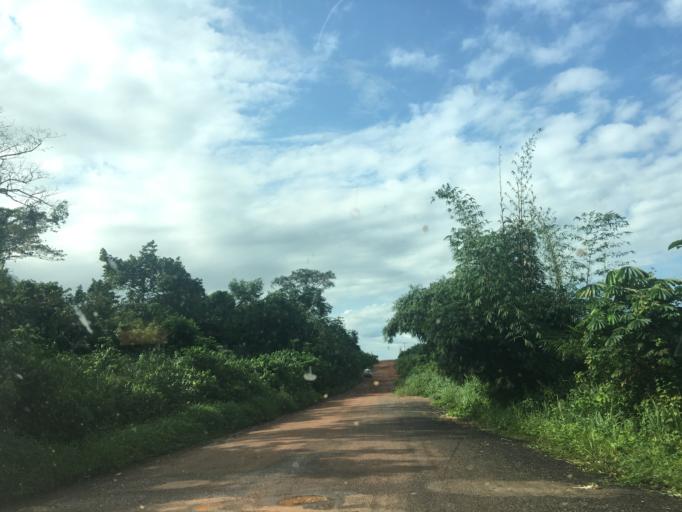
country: GH
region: Western
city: Wassa-Akropong
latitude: 5.9794
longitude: -2.4152
